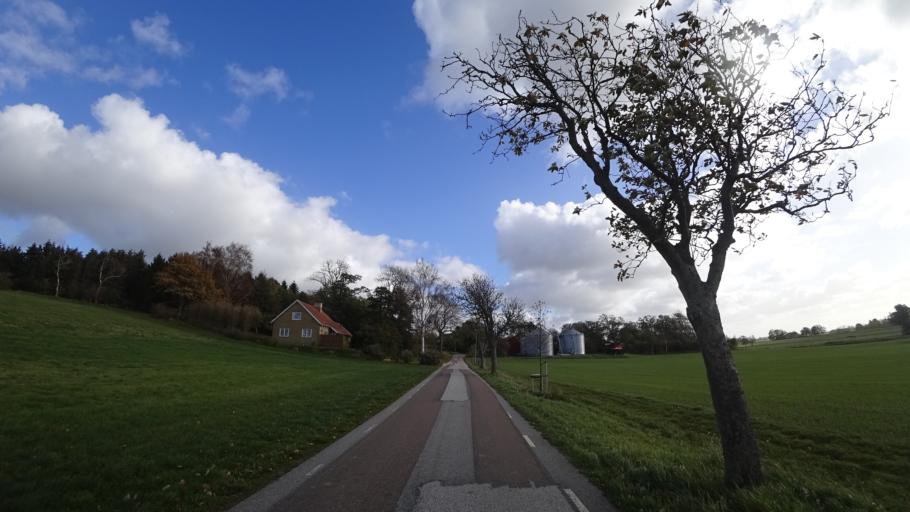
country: SE
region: Skane
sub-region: Staffanstorps Kommun
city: Staffanstorp
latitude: 55.6344
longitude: 13.1658
